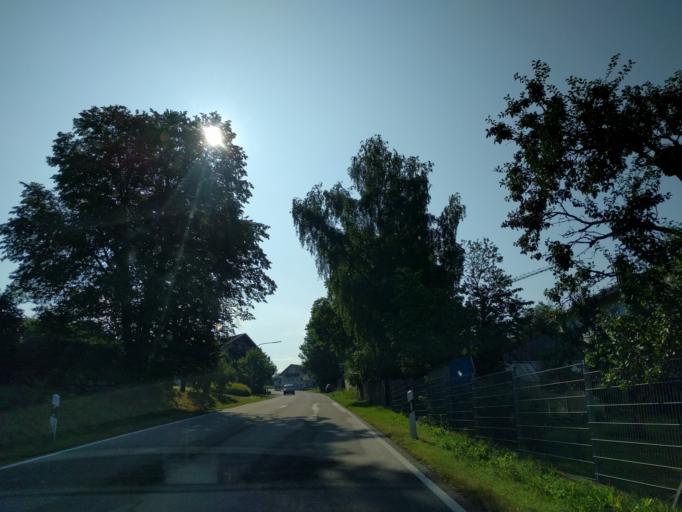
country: DE
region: Bavaria
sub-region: Lower Bavaria
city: Grafenau
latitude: 48.8517
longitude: 13.4143
